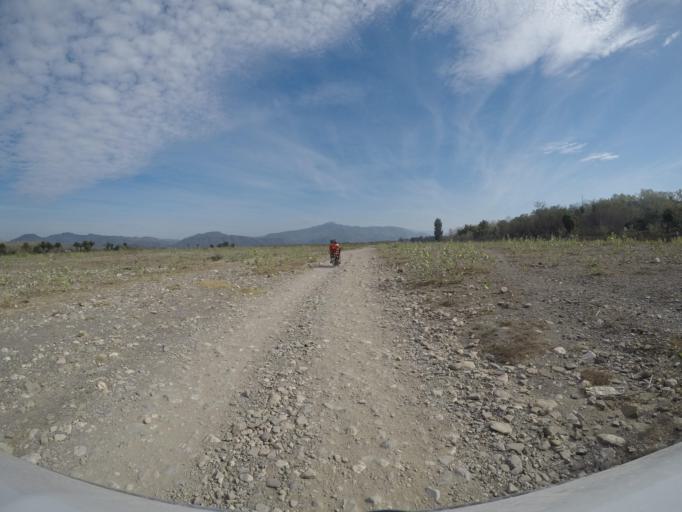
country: TL
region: Bobonaro
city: Maliana
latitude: -8.8927
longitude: 125.2083
